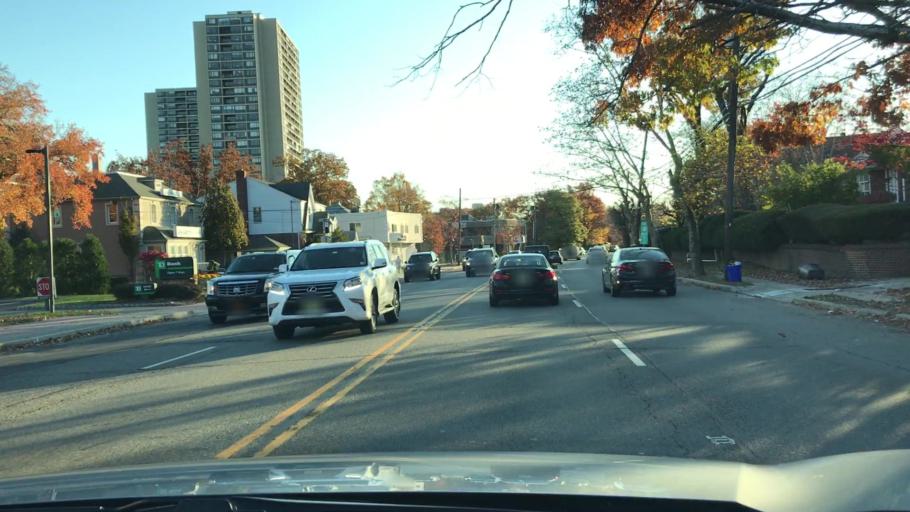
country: US
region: New Jersey
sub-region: Bergen County
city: Fort Lee
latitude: 40.8436
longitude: -73.9729
